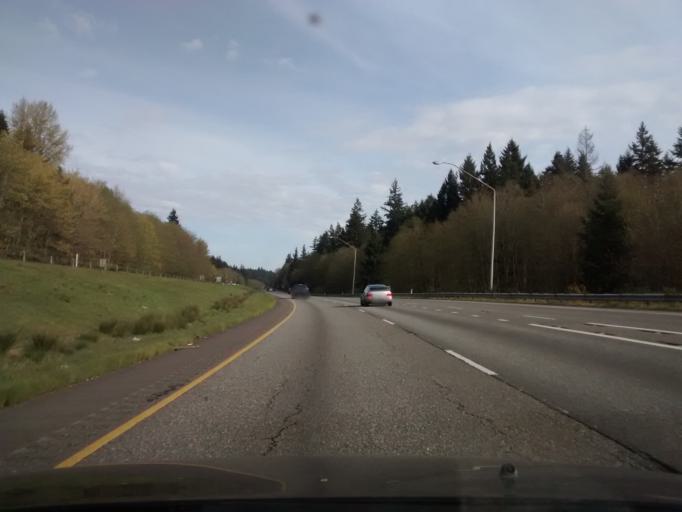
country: US
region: Washington
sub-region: Kitsap County
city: Silverdale
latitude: 47.6412
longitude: -122.7047
